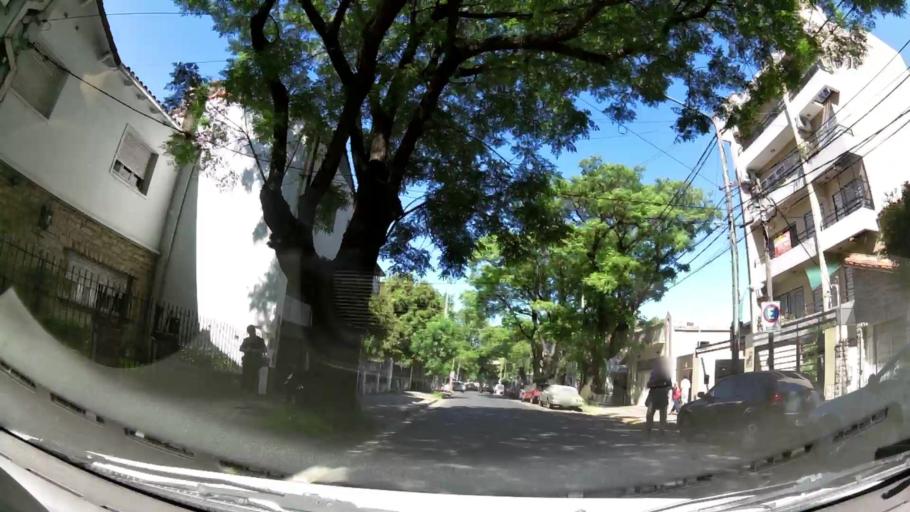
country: AR
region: Buenos Aires
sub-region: Partido de Vicente Lopez
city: Olivos
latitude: -34.5218
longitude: -58.4872
